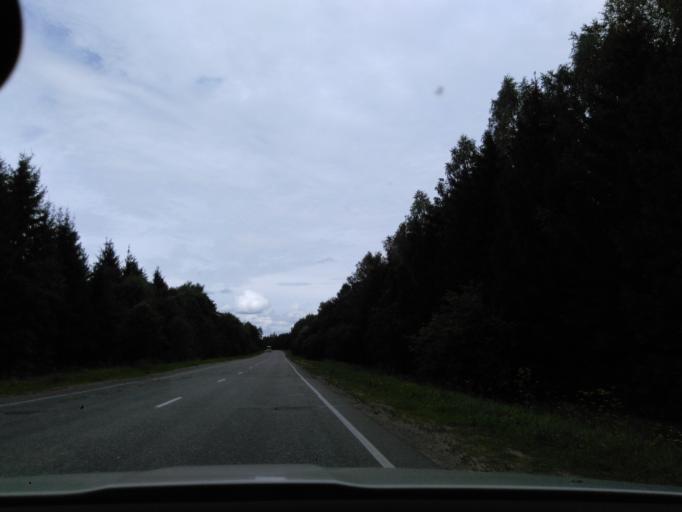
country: RU
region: Tverskaya
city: Konakovo
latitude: 56.6592
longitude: 36.7159
